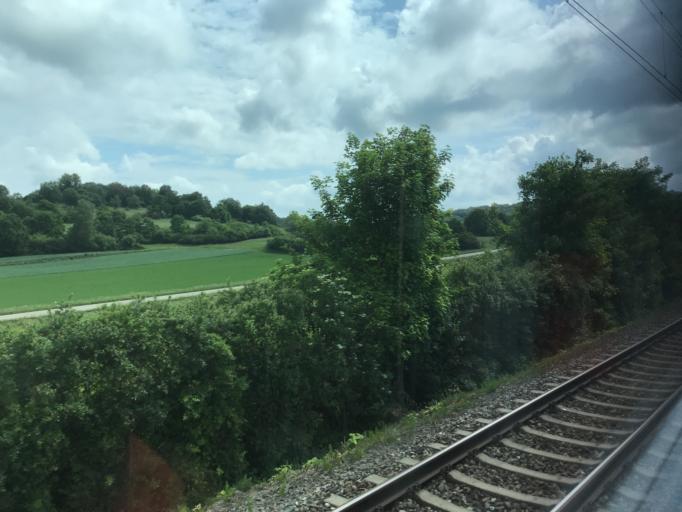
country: DE
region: Baden-Wuerttemberg
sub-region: Tuebingen Region
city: Lonsee
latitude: 48.5316
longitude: 9.9286
